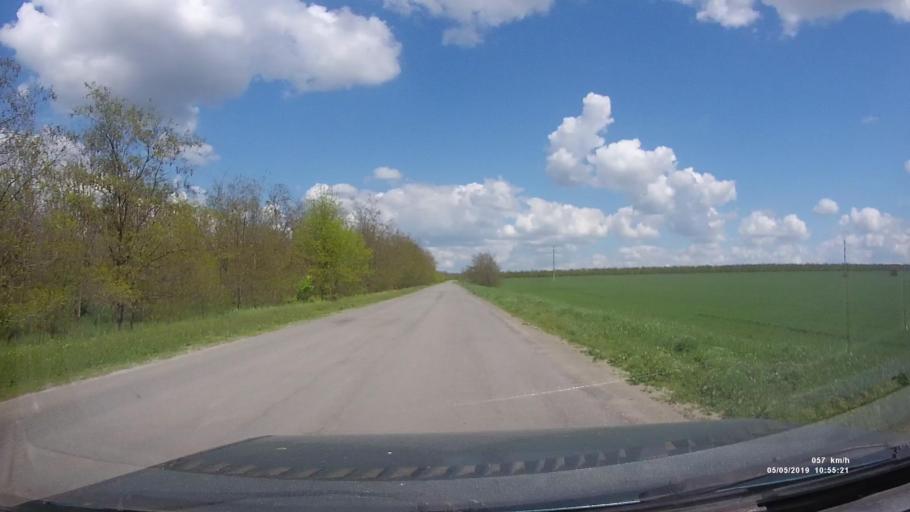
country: RU
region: Rostov
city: Ust'-Donetskiy
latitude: 47.6648
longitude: 40.8213
